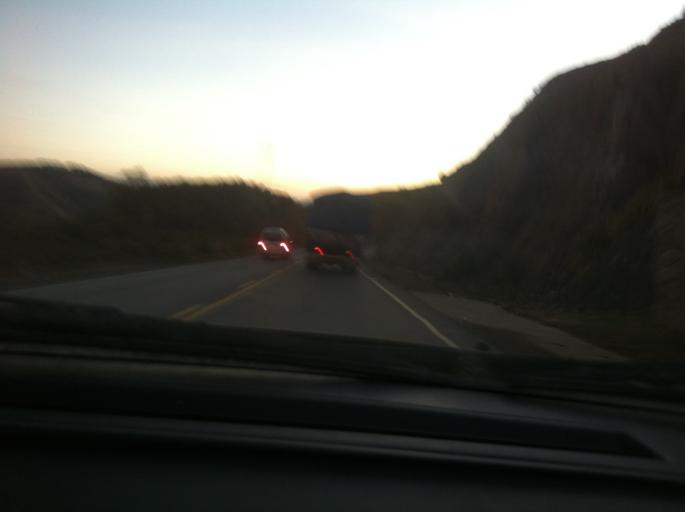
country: BO
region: Cochabamba
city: Irpa Irpa
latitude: -17.6547
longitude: -66.4018
